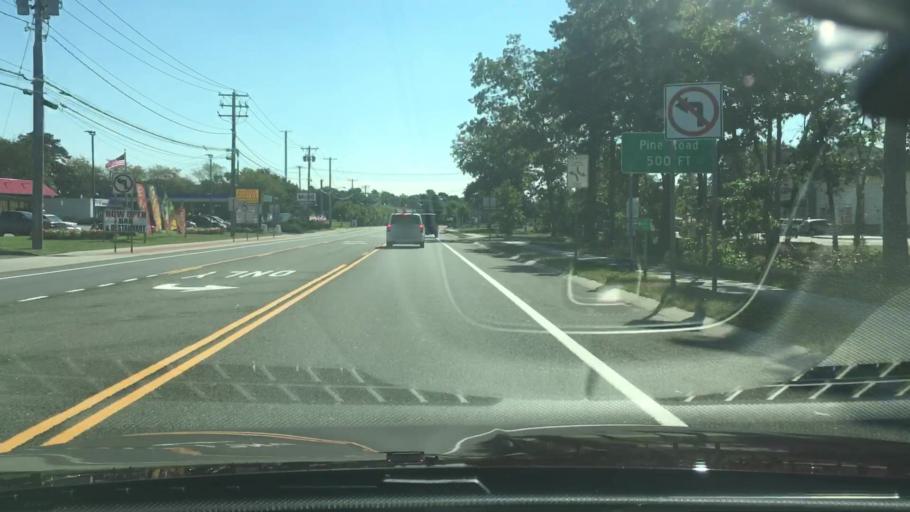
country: US
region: New York
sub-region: Suffolk County
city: Coram
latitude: 40.8925
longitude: -73.0155
